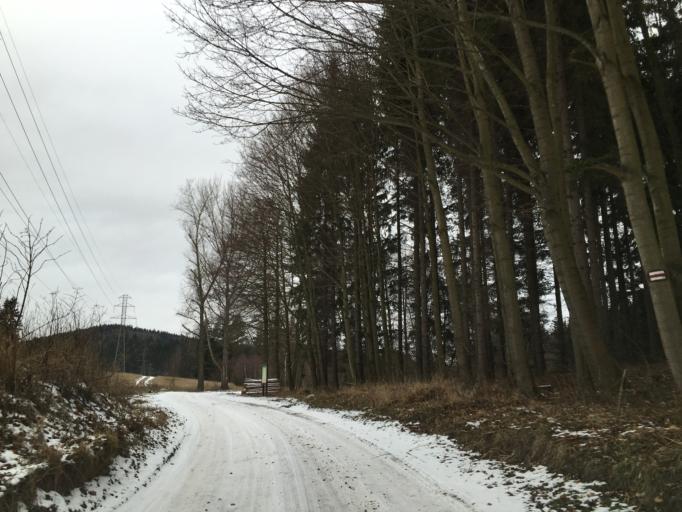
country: PL
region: Lower Silesian Voivodeship
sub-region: Powiat kamiennogorski
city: Krzeszow
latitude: 50.6928
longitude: 16.1047
